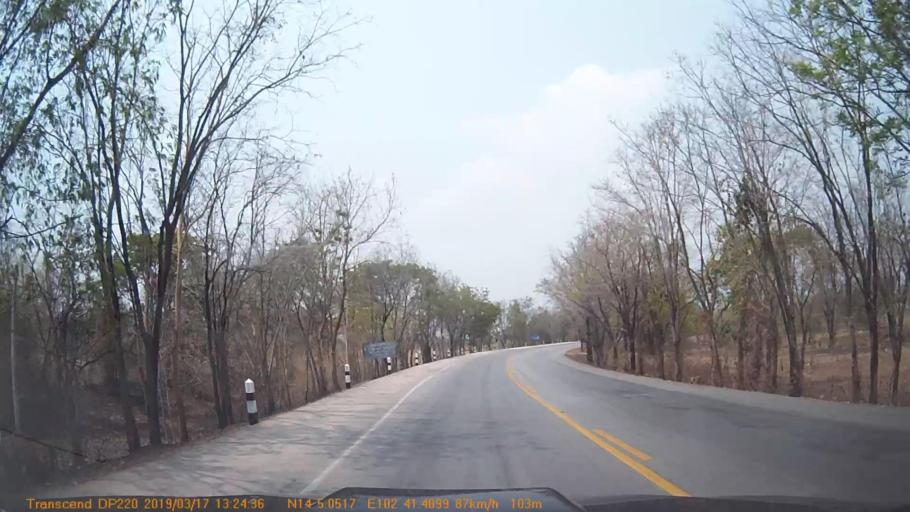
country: TH
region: Sa Kaeo
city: Ta Phraya
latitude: 14.0846
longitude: 102.6901
